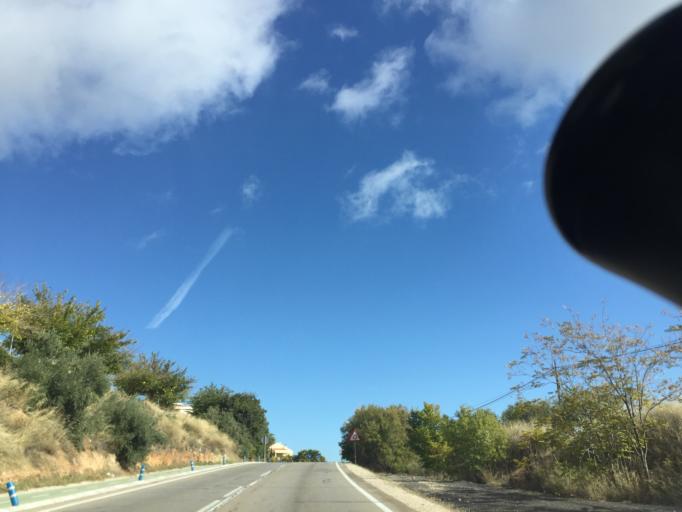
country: ES
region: Andalusia
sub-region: Provincia de Jaen
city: Jaen
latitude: 37.7548
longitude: -3.7955
